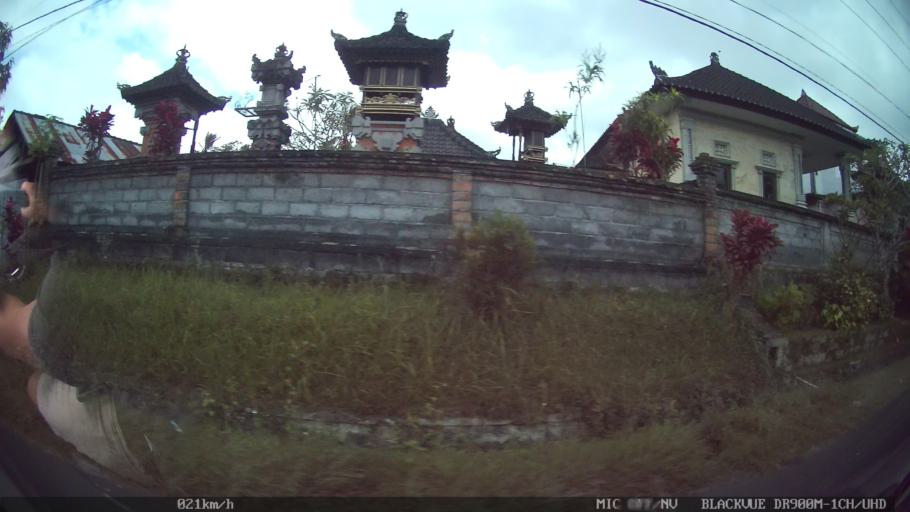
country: ID
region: Bali
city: Banjar Petak
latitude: -8.4443
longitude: 115.3190
